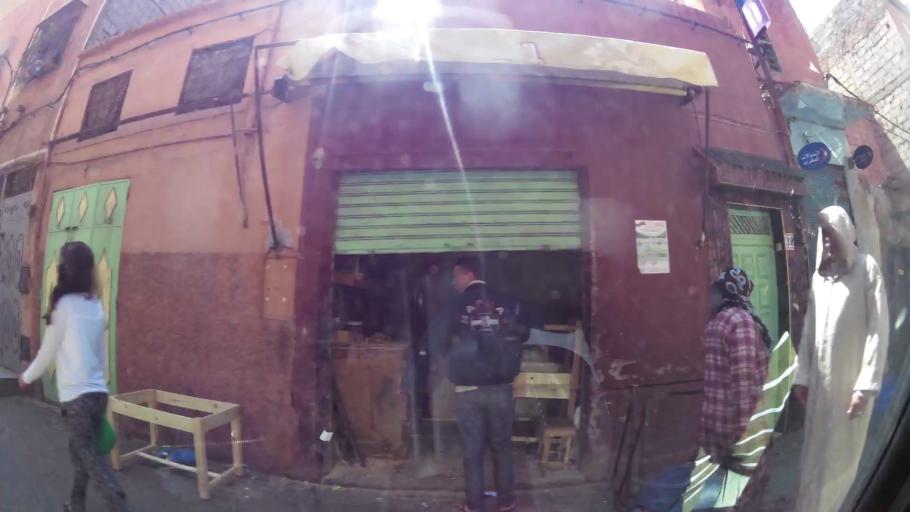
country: MA
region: Marrakech-Tensift-Al Haouz
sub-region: Marrakech
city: Marrakesh
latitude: 31.6191
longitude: -7.9706
